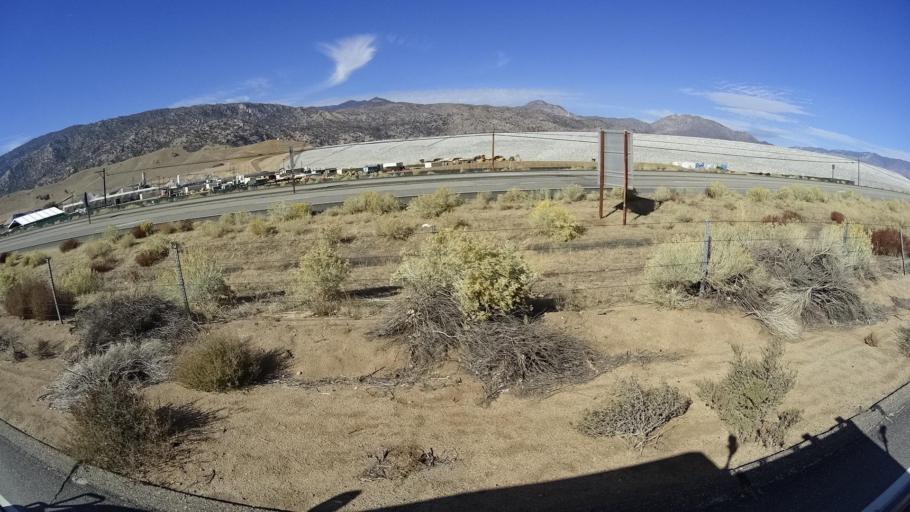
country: US
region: California
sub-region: Kern County
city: Lake Isabella
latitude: 35.6388
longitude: -118.4659
